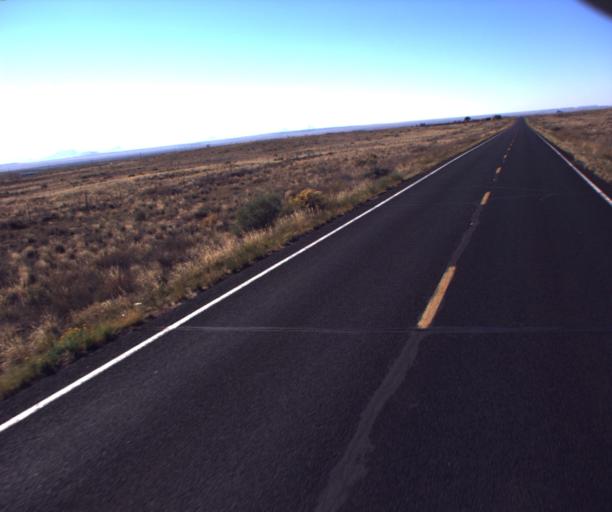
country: US
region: Arizona
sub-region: Navajo County
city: First Mesa
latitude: 35.7807
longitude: -110.5017
